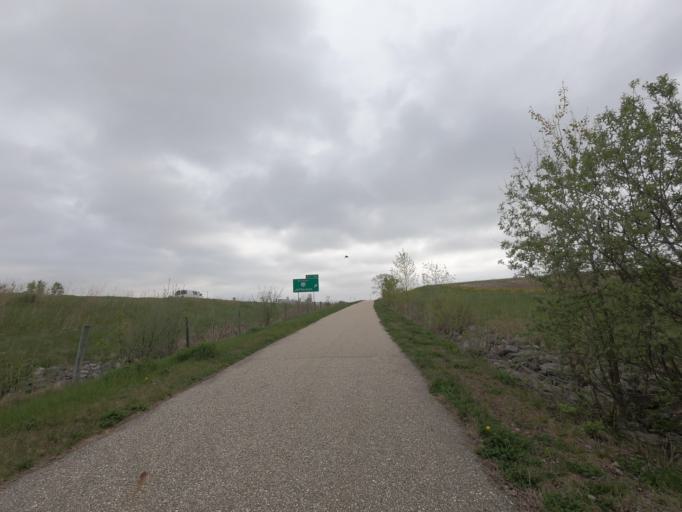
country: US
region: Wisconsin
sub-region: Jefferson County
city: Jefferson
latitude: 43.0307
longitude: -88.8108
